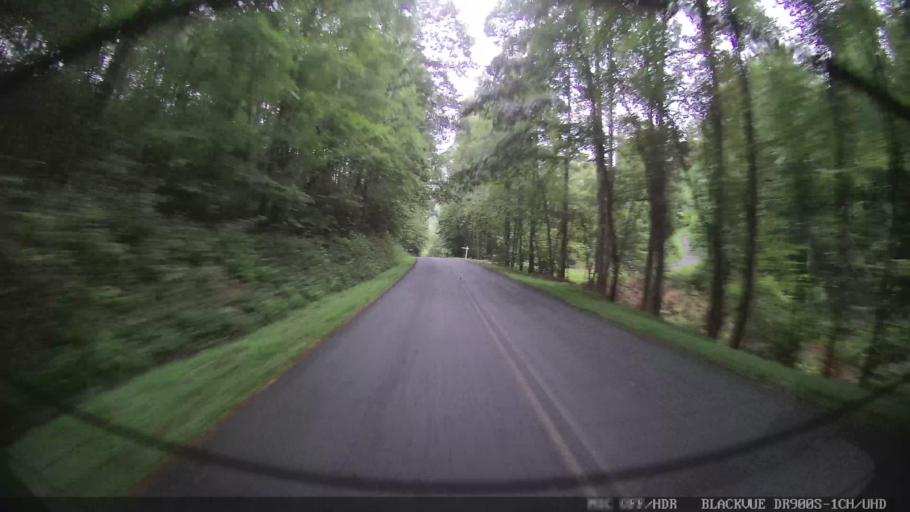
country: US
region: Georgia
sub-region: Gilmer County
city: Ellijay
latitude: 34.7778
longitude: -84.5410
